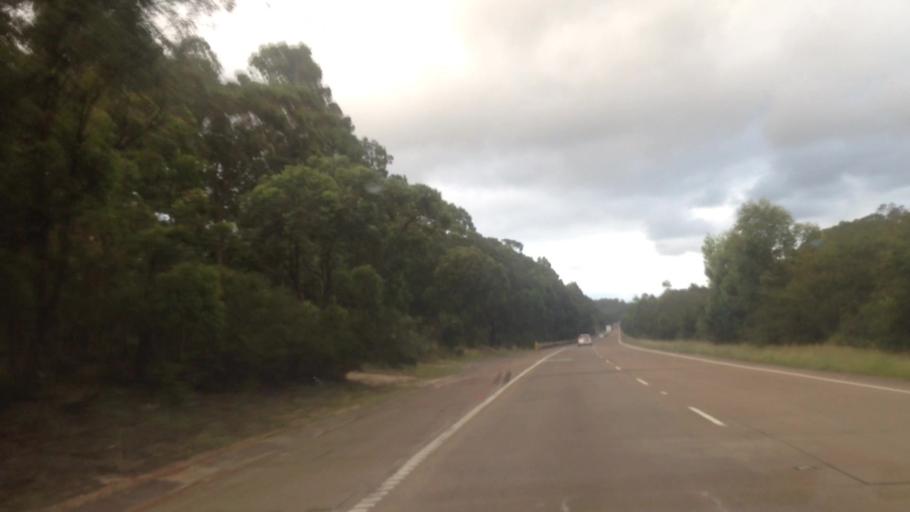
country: AU
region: New South Wales
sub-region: Wyong Shire
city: Charmhaven
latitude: -33.1702
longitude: 151.4670
